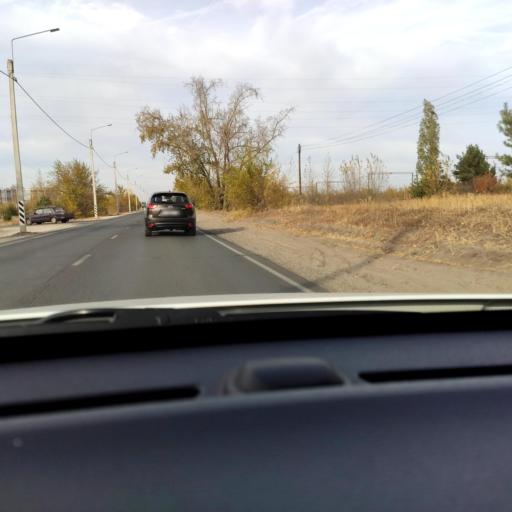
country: RU
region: Voronezj
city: Maslovka
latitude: 51.5762
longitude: 39.2469
